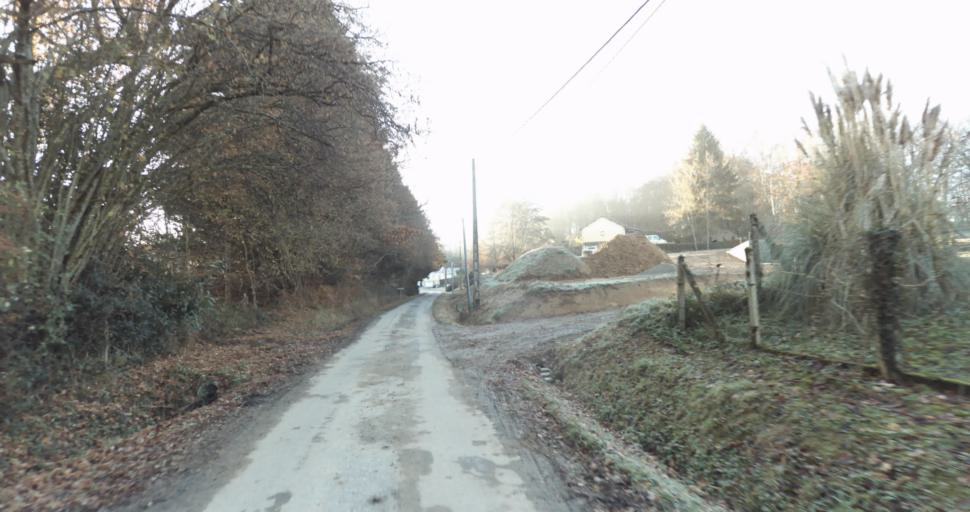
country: FR
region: Limousin
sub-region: Departement de la Haute-Vienne
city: Aixe-sur-Vienne
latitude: 45.8193
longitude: 1.1498
